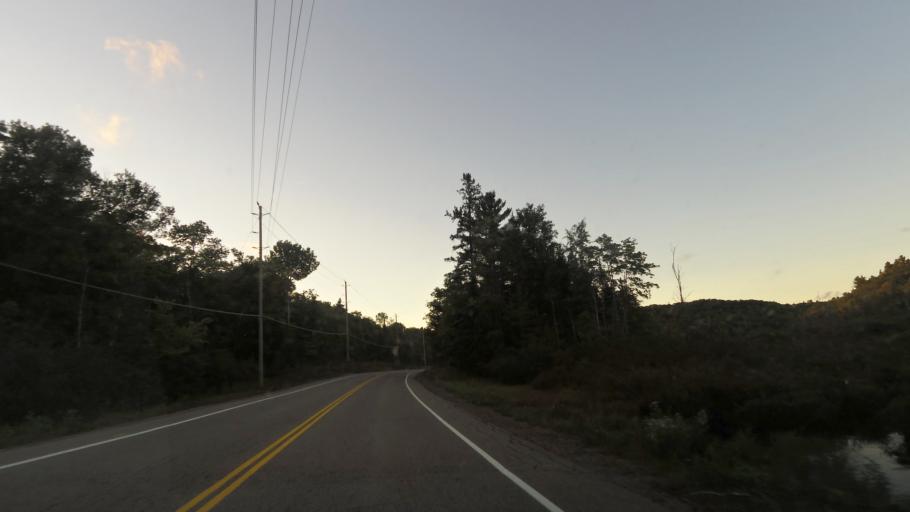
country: CA
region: Ontario
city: Bancroft
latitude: 45.0358
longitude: -78.4154
